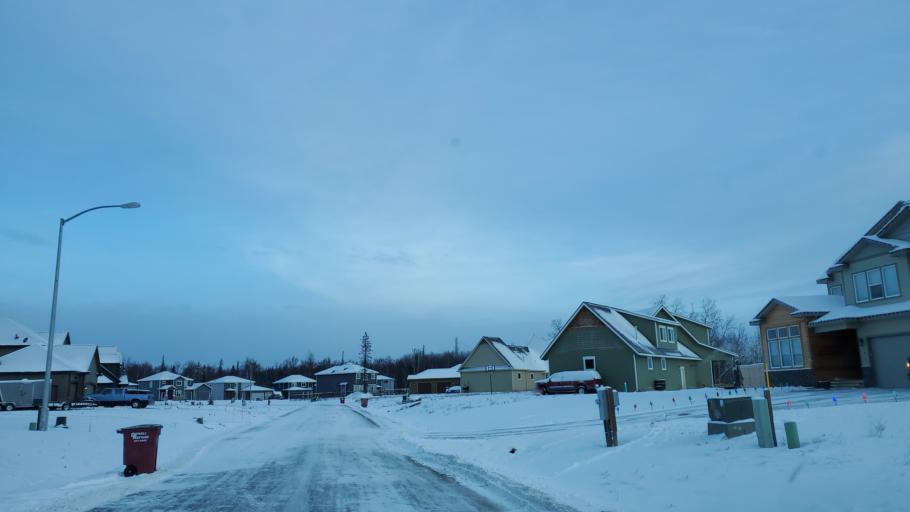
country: US
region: Alaska
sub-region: Matanuska-Susitna Borough
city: Lakes
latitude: 61.5447
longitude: -149.3215
